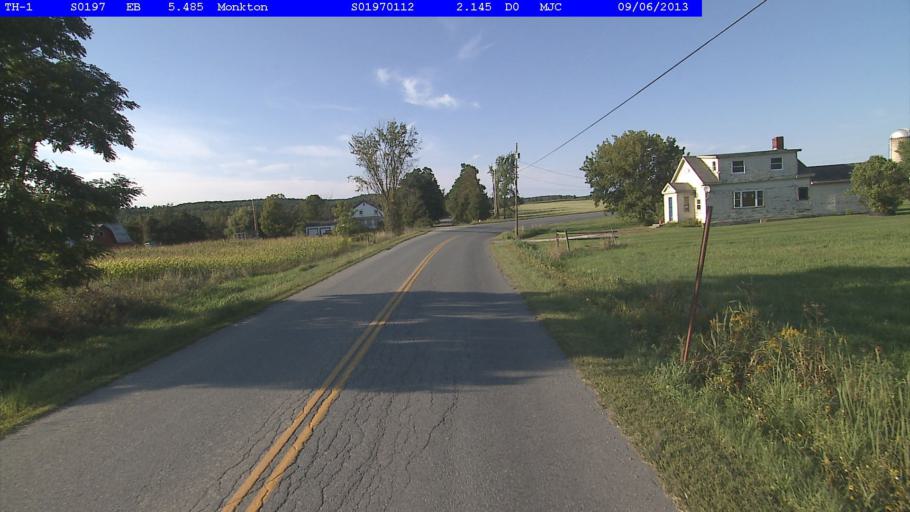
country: US
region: Vermont
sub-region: Addison County
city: Vergennes
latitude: 44.2133
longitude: -73.1641
